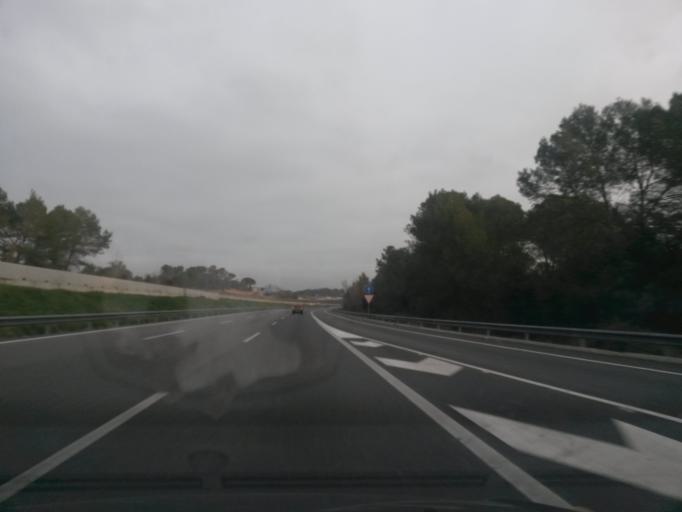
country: ES
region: Catalonia
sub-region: Provincia de Girona
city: Cervia de Ter
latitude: 42.0815
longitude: 2.8900
